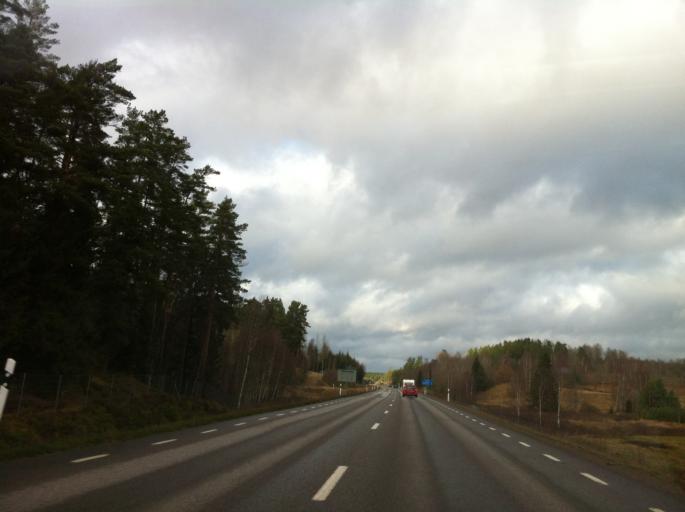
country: SE
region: Kalmar
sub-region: Vimmerby Kommun
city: Vimmerby
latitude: 57.5931
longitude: 15.8482
